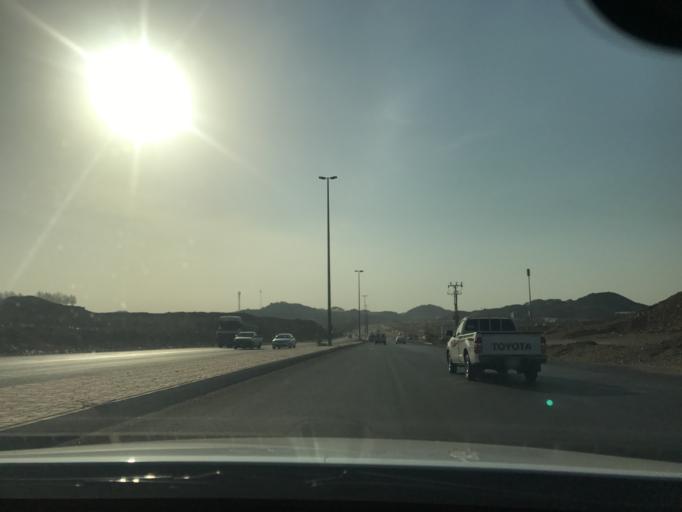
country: SA
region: Makkah
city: Jeddah
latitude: 21.4128
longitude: 39.4190
